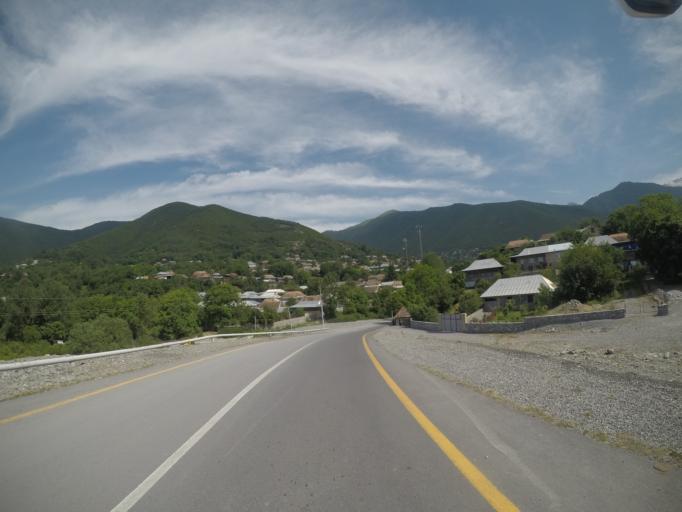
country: AZ
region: Shaki City
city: Sheki
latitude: 41.2459
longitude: 47.1887
